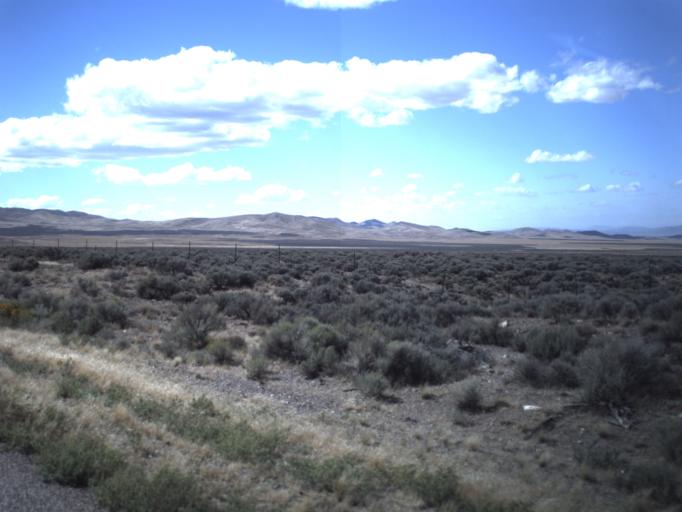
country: US
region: Utah
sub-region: Beaver County
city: Milford
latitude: 38.1736
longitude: -112.9507
